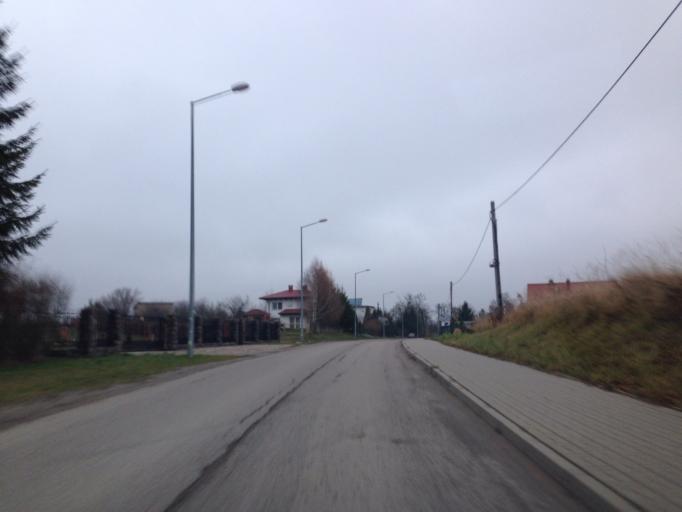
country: PL
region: Warmian-Masurian Voivodeship
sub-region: Powiat ketrzynski
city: Ketrzyn
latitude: 54.0603
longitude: 21.3764
